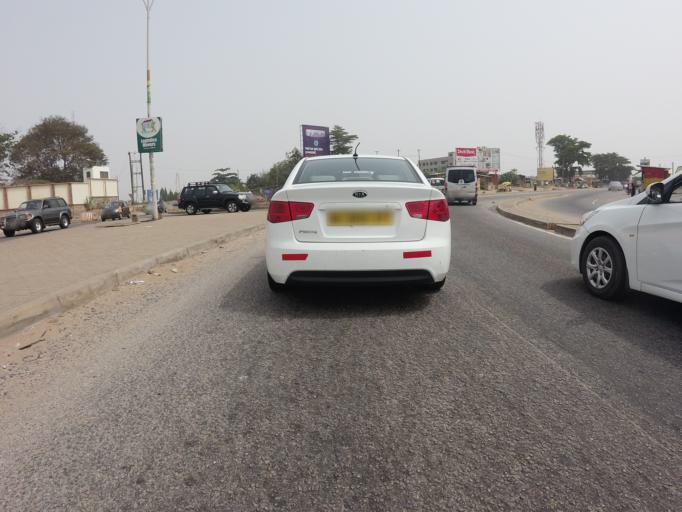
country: GH
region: Greater Accra
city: Medina Estates
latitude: 5.6268
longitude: -0.1536
